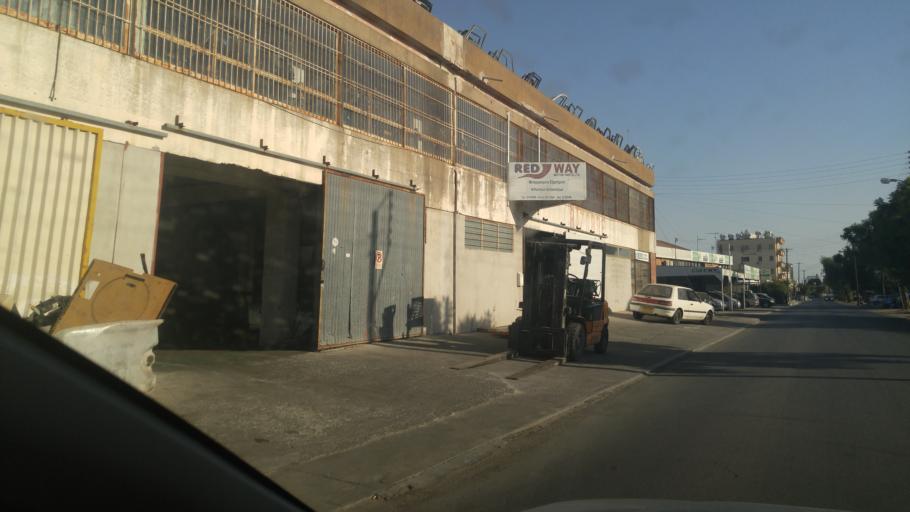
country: CY
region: Limassol
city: Limassol
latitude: 34.6730
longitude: 33.0220
